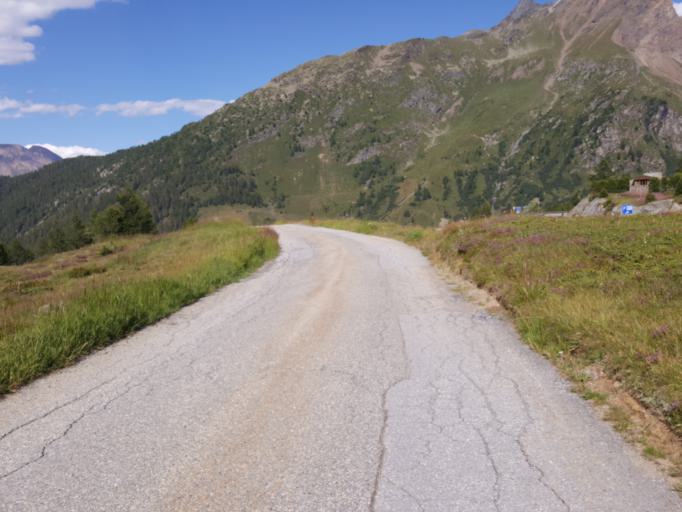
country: CH
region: Valais
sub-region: Brig District
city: Brig
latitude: 46.2500
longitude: 8.0300
